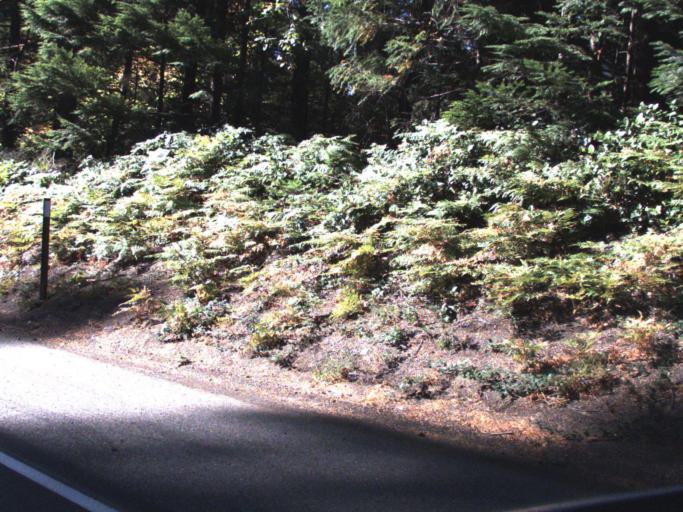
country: US
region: Washington
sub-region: Pierce County
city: Buckley
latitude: 46.6930
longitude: -121.5707
